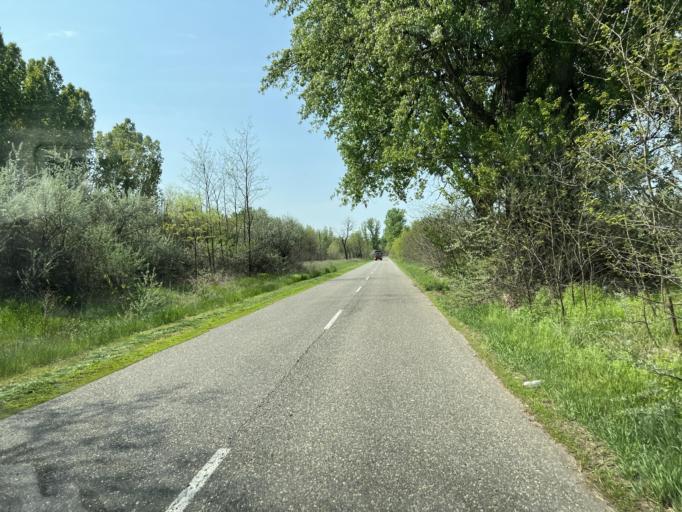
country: HU
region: Pest
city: Tortel
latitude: 47.0715
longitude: 19.8668
